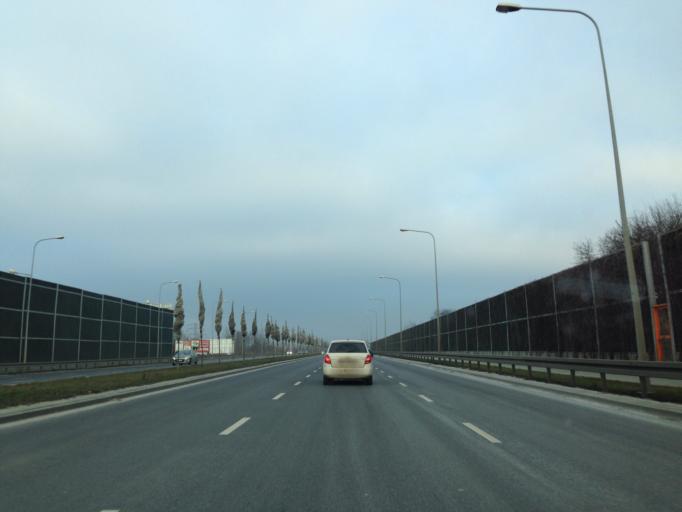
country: PL
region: Greater Poland Voivodeship
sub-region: Poznan
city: Poznan
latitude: 52.4157
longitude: 16.9576
